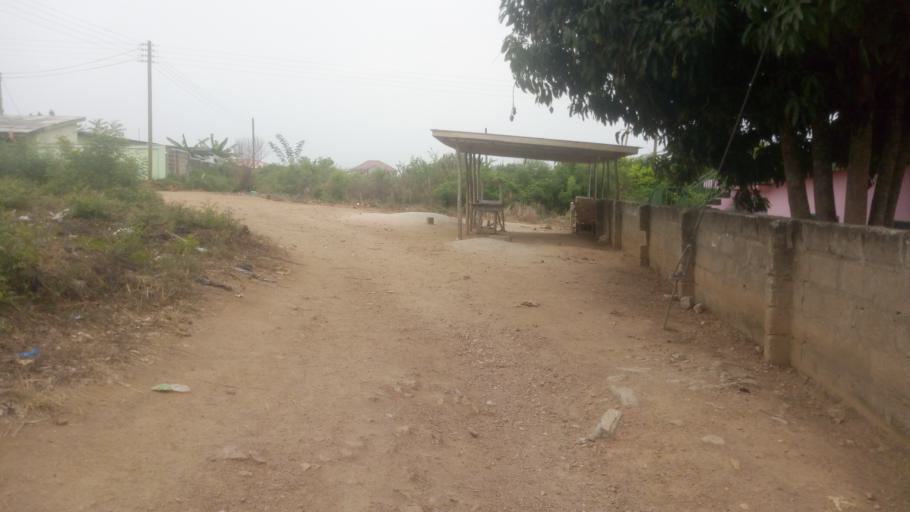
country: GH
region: Central
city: Winneba
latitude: 5.3595
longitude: -0.6260
